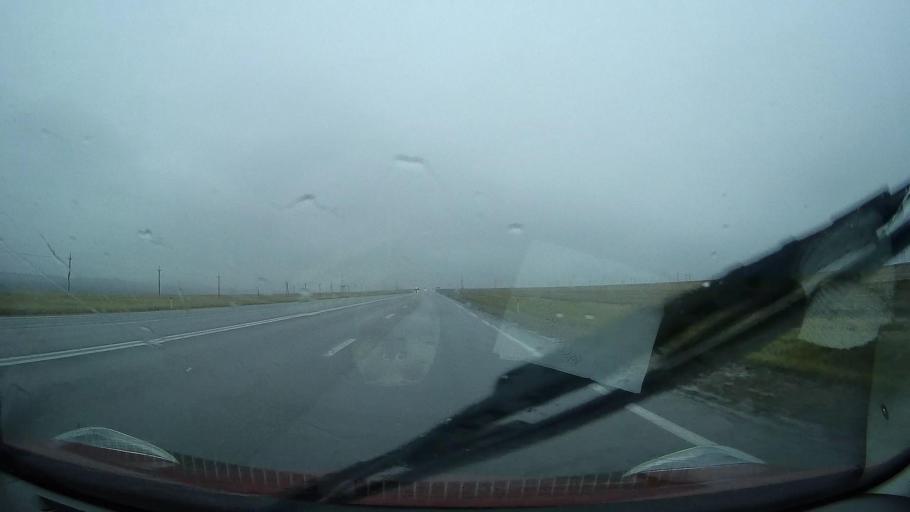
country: RU
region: Stavropol'skiy
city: Kursavka
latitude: 44.5813
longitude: 42.2421
